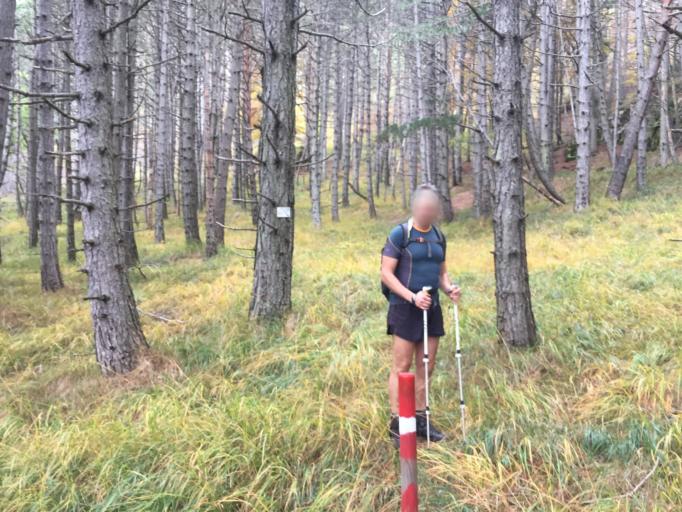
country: IT
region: Friuli Venezia Giulia
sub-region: Provincia di Udine
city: Chiusaforte
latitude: 46.4149
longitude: 13.3025
